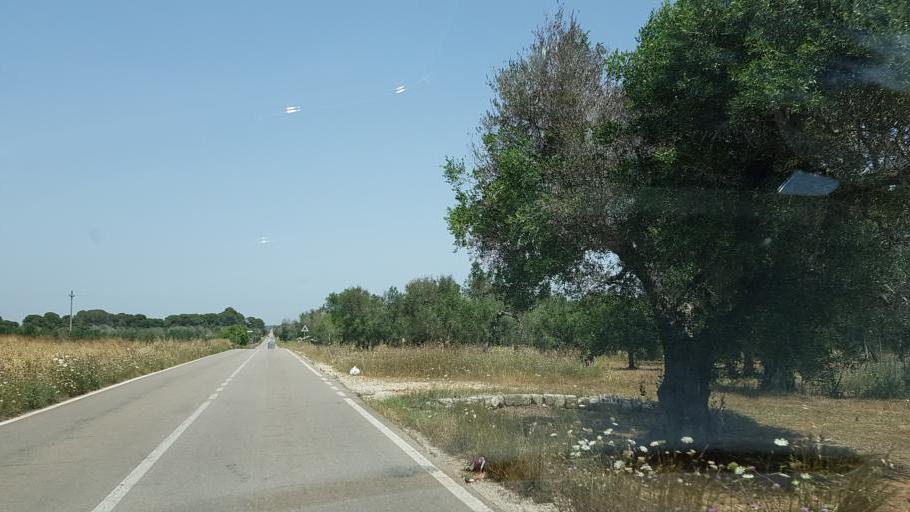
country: IT
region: Apulia
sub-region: Provincia di Lecce
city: Porto Cesareo
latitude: 40.3033
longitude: 17.9179
